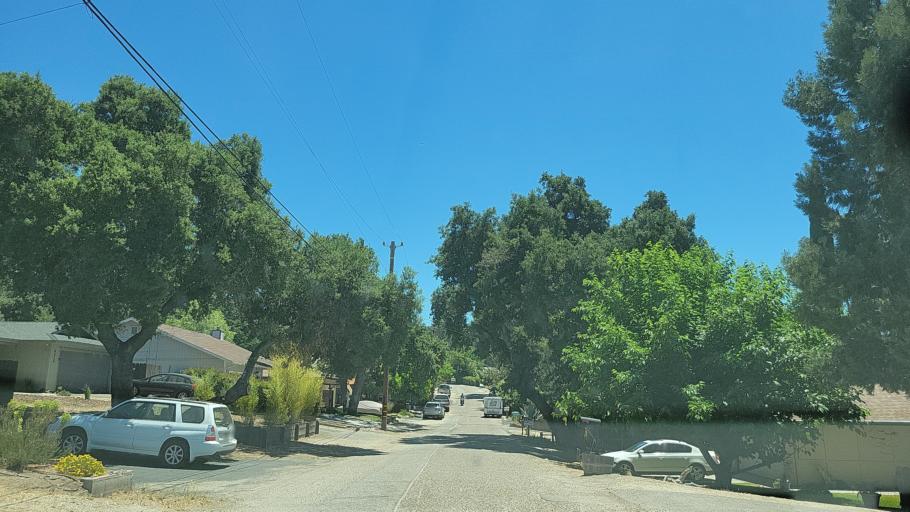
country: US
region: California
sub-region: San Luis Obispo County
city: Atascadero
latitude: 35.5010
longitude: -120.6816
